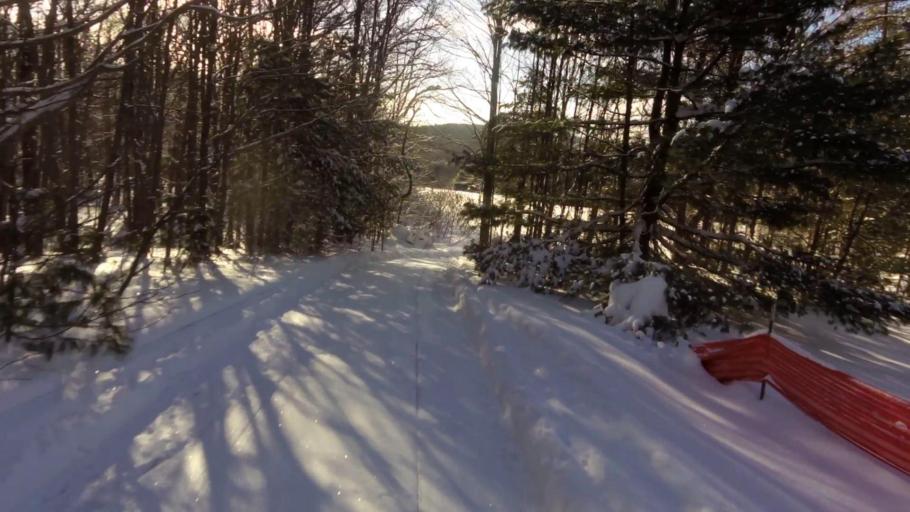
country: US
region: New York
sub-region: Chautauqua County
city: Falconer
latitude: 42.2569
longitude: -79.1711
